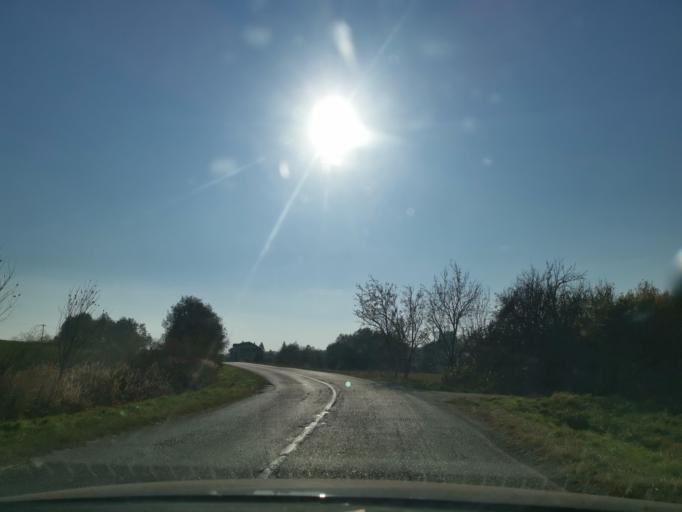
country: SK
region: Trnavsky
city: Gbely
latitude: 48.6883
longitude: 17.2035
